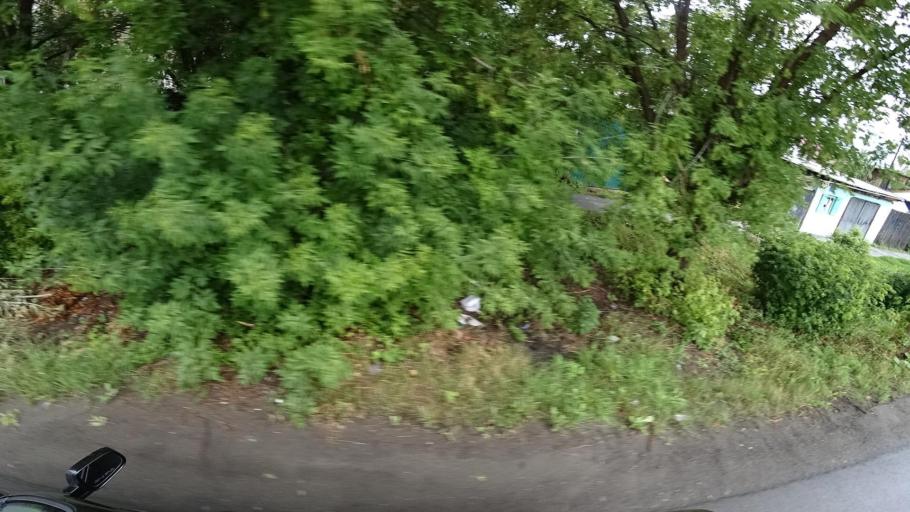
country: RU
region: Sverdlovsk
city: Kamyshlov
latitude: 56.8445
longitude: 62.7200
